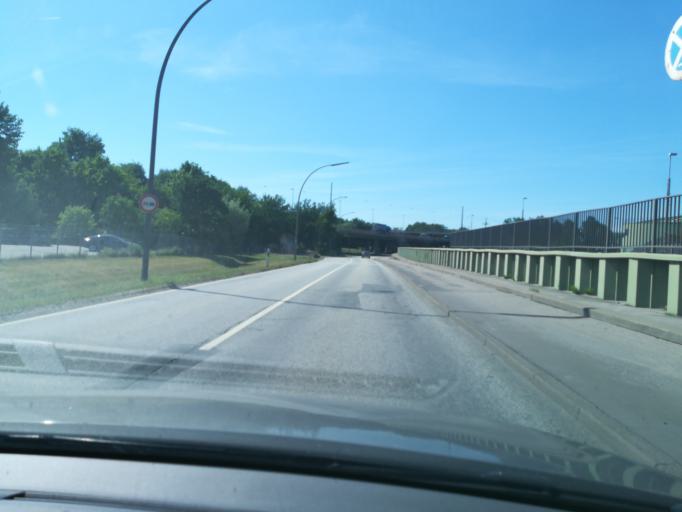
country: DE
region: Hamburg
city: Rothenburgsort
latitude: 53.5159
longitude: 10.0328
